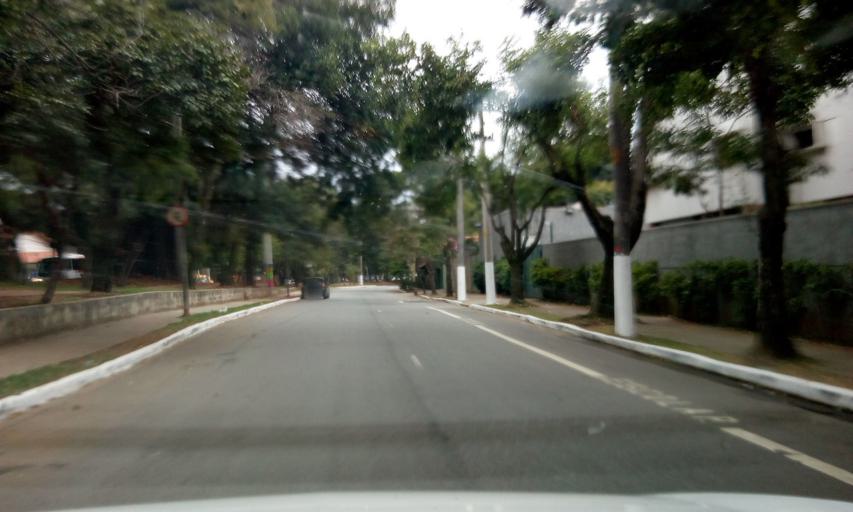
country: BR
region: Sao Paulo
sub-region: Osasco
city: Osasco
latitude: -23.5494
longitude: -46.7169
